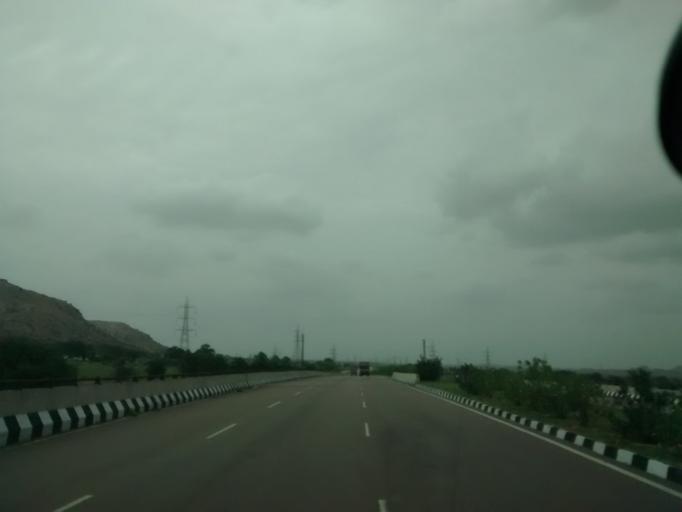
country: IN
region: Andhra Pradesh
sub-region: Kurnool
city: Ramapuram
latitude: 15.1103
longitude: 77.6610
